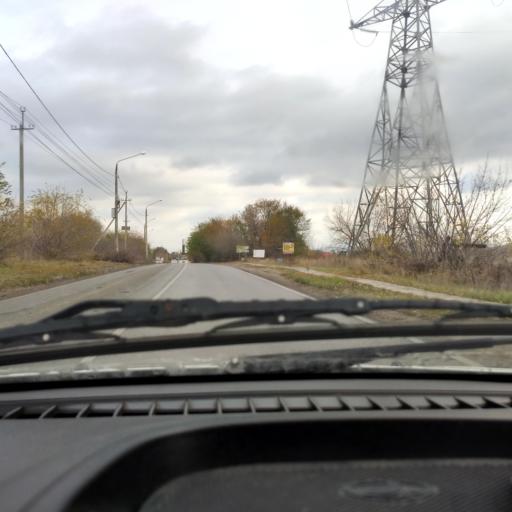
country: RU
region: Samara
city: Zhigulevsk
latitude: 53.4629
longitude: 49.5736
